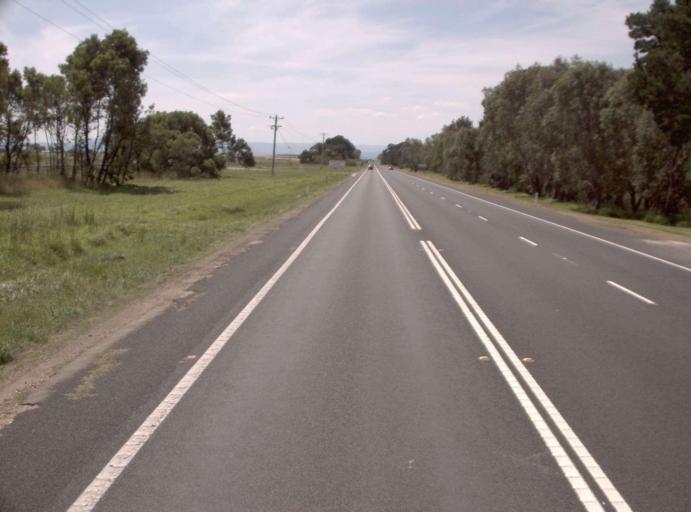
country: AU
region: Victoria
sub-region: Wellington
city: Sale
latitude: -38.0449
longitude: 147.0634
